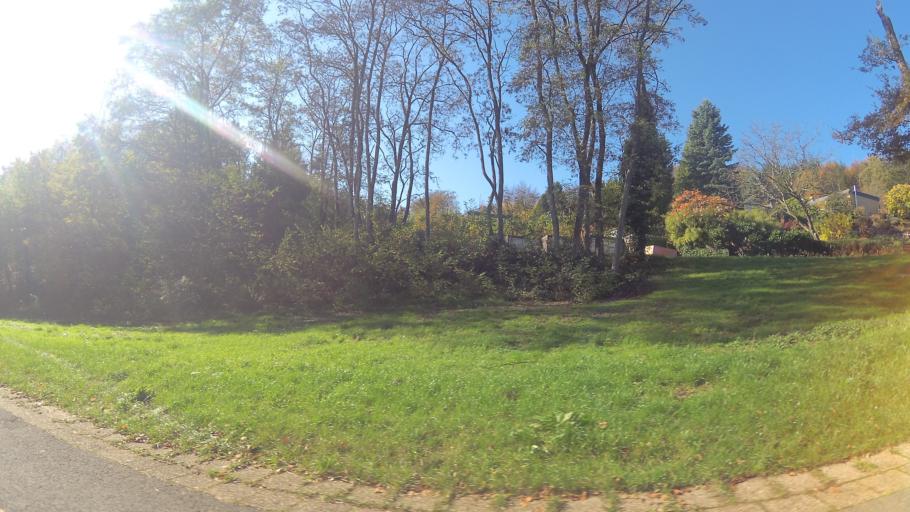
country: DE
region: Saarland
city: Losheim
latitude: 49.5426
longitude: 6.7738
